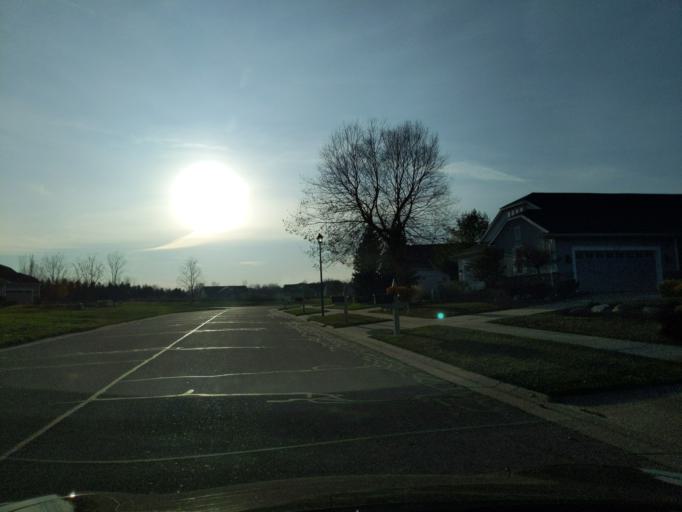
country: US
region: Michigan
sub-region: Clinton County
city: Bath
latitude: 42.7950
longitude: -84.4598
